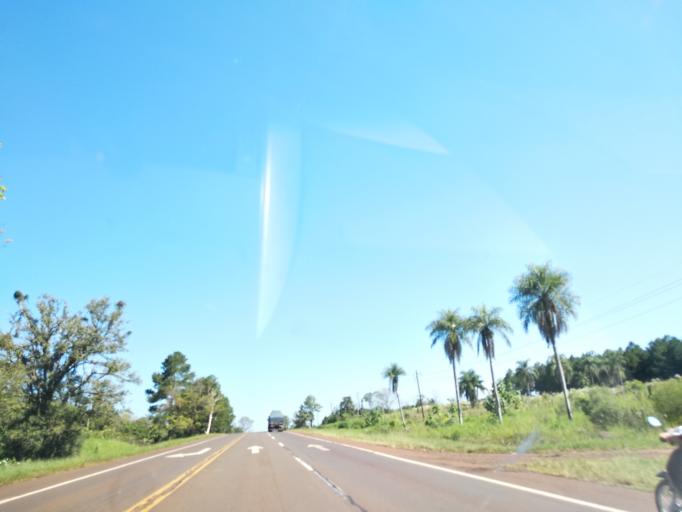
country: AR
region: Misiones
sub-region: Departamento de Eldorado
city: Eldorado
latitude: -26.3631
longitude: -54.6214
